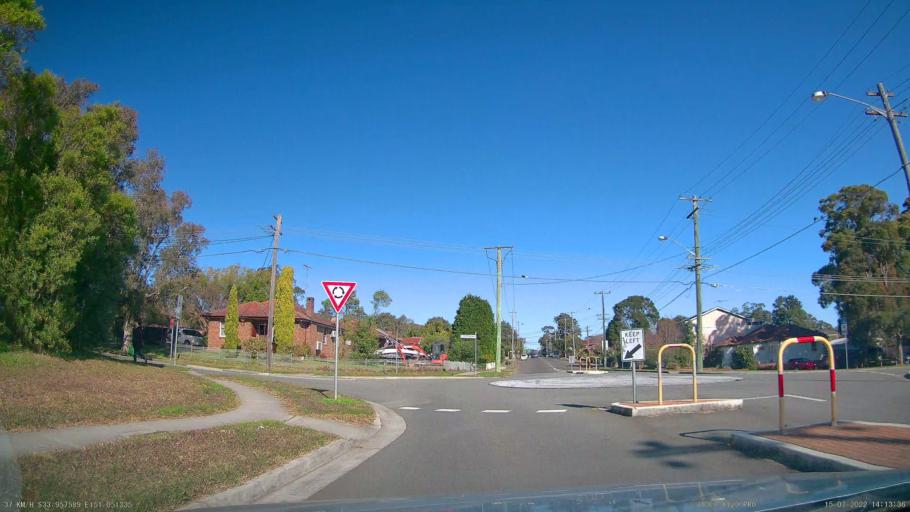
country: AU
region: New South Wales
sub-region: Hurstville
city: Peakhurst
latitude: -33.9577
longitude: 151.0513
